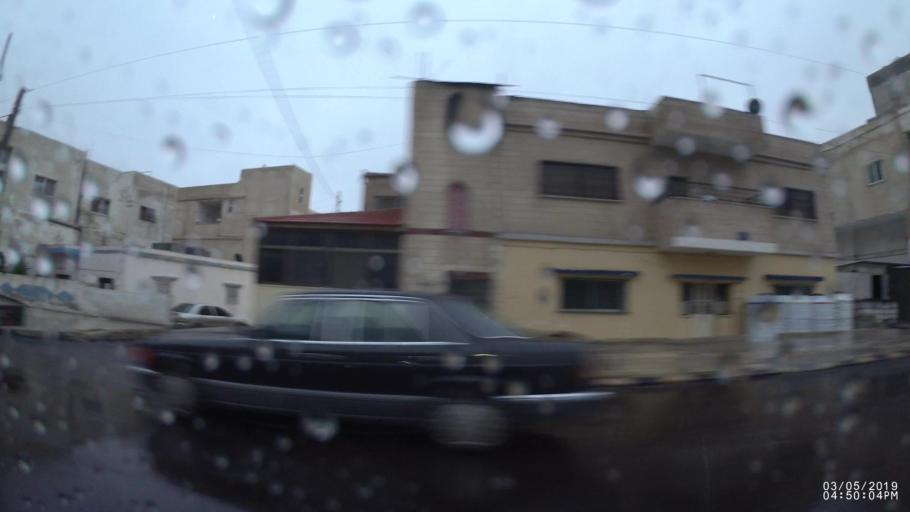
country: JO
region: Amman
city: Amman
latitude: 32.0019
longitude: 35.9671
